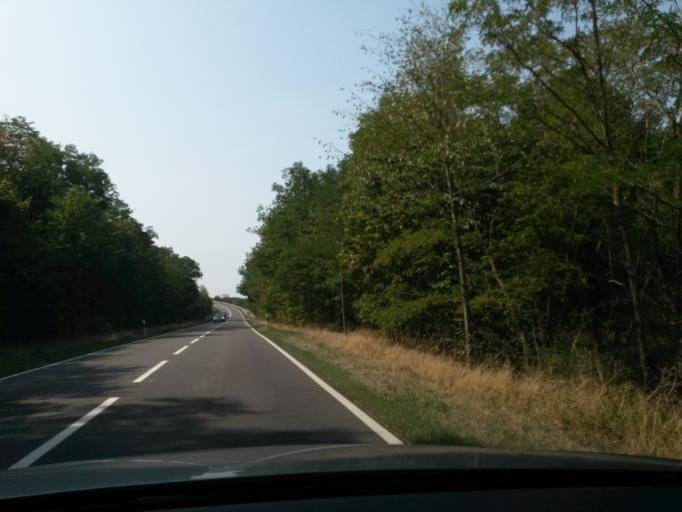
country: DE
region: Saxony-Anhalt
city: Hohenwarthe
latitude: 52.2406
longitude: 11.7321
